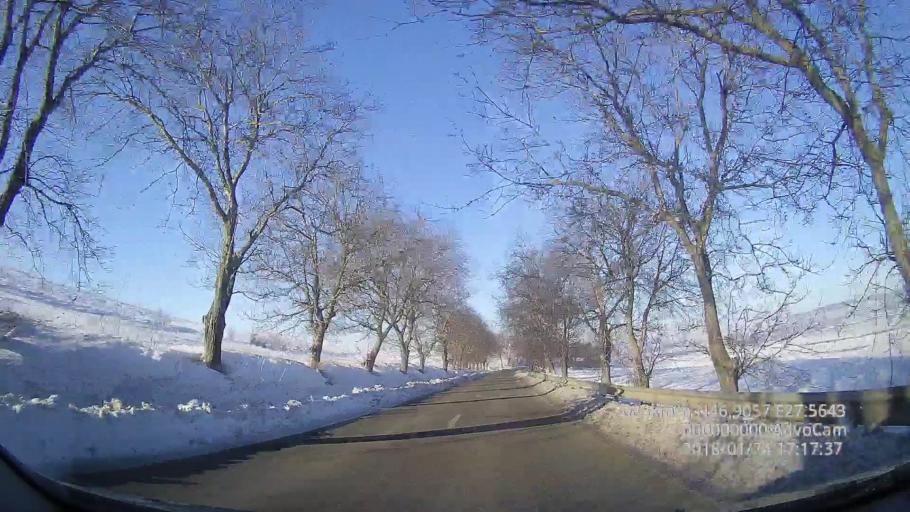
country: RO
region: Iasi
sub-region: Comuna Scanteia
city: Scanteia
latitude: 46.9065
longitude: 27.5642
